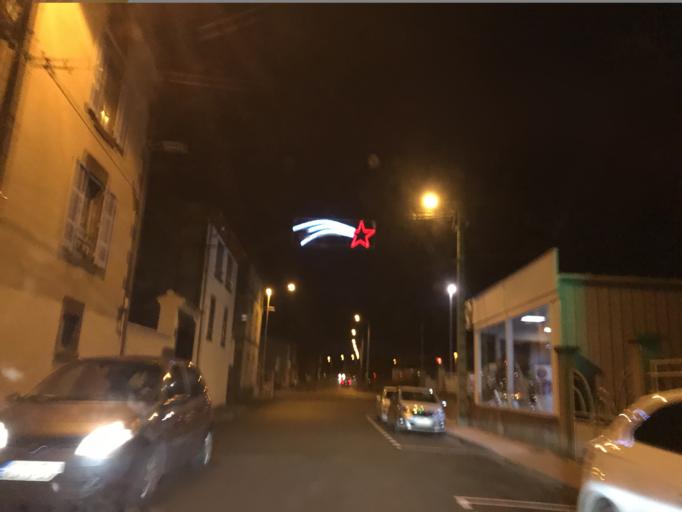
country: FR
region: Auvergne
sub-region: Departement du Puy-de-Dome
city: Cournon-d'Auvergne
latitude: 45.7394
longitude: 3.2000
